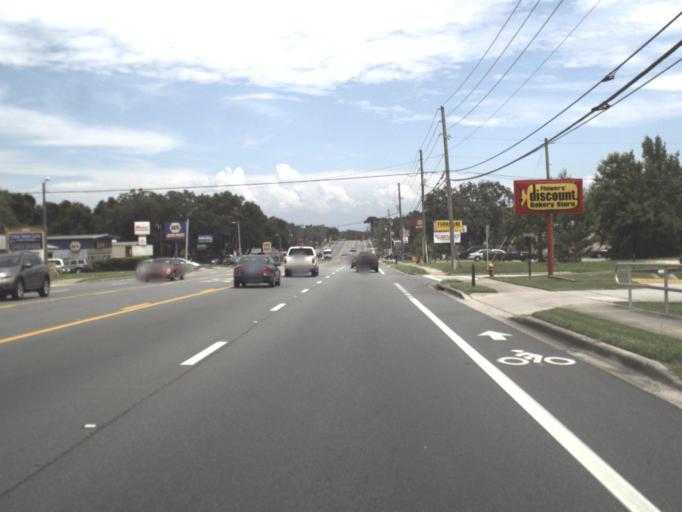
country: US
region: Florida
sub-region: Citrus County
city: Inverness Highlands North
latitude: 28.8414
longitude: -82.3620
